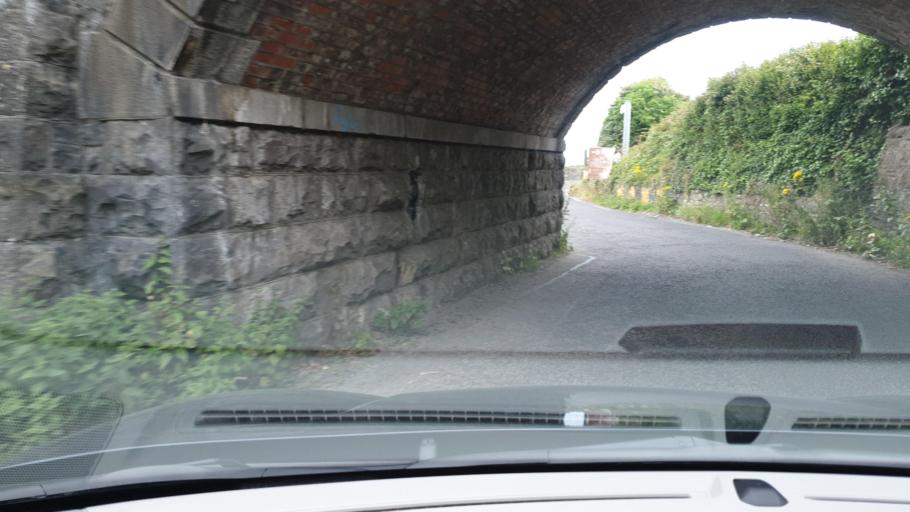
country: IE
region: Leinster
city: Balrothery
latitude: 53.5850
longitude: -6.1481
